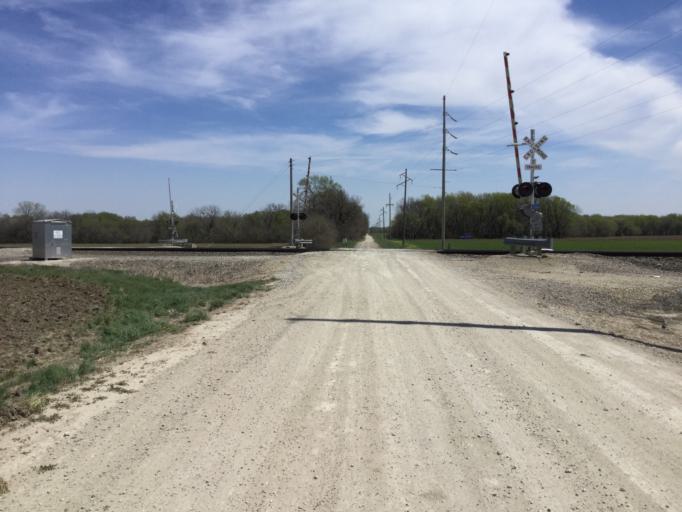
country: US
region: Kansas
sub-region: Butler County
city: Augusta
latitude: 37.7084
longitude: -96.9356
